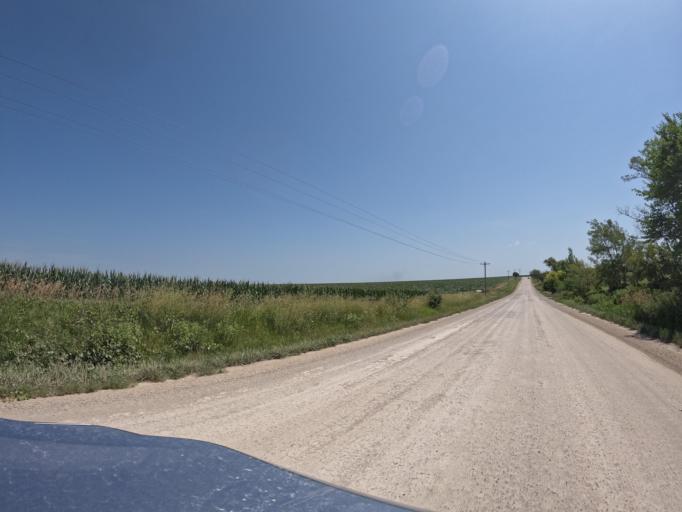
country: US
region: Iowa
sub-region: Henry County
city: Mount Pleasant
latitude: 40.9375
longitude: -91.5207
